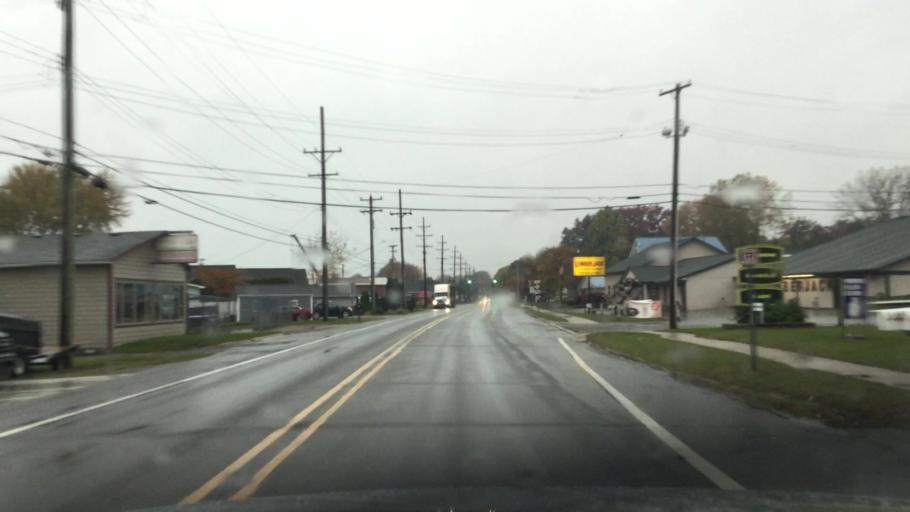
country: US
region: Michigan
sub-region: Saint Clair County
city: Algonac
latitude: 42.6180
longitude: -82.5579
